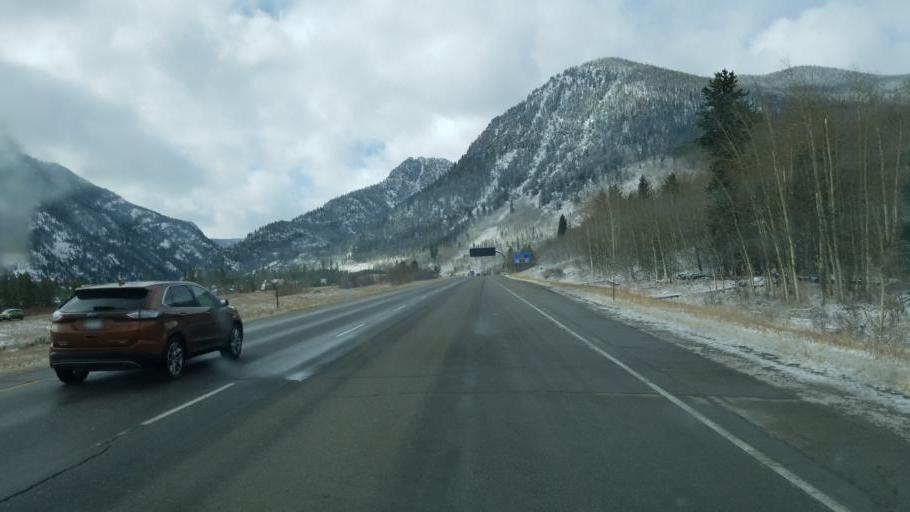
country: US
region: Colorado
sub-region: Summit County
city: Frisco
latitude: 39.5898
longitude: -106.1017
